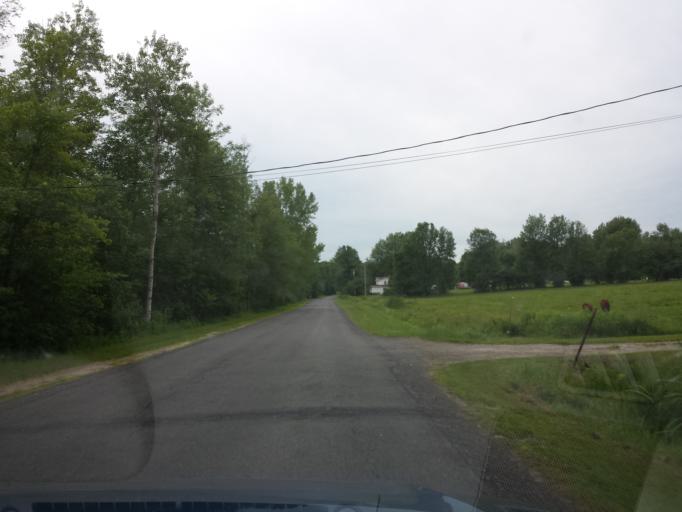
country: US
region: New York
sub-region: St. Lawrence County
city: Norwood
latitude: 44.7268
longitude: -74.9464
